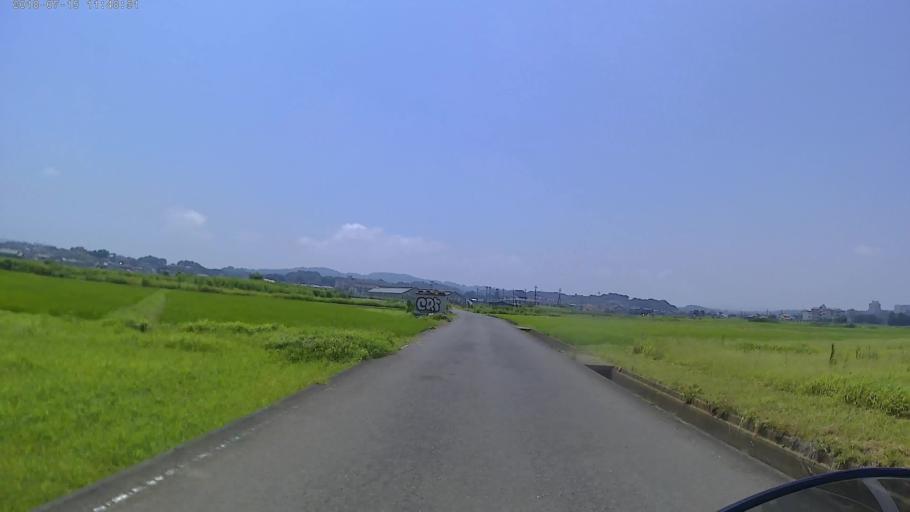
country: JP
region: Kanagawa
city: Isehara
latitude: 35.3658
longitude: 139.2944
